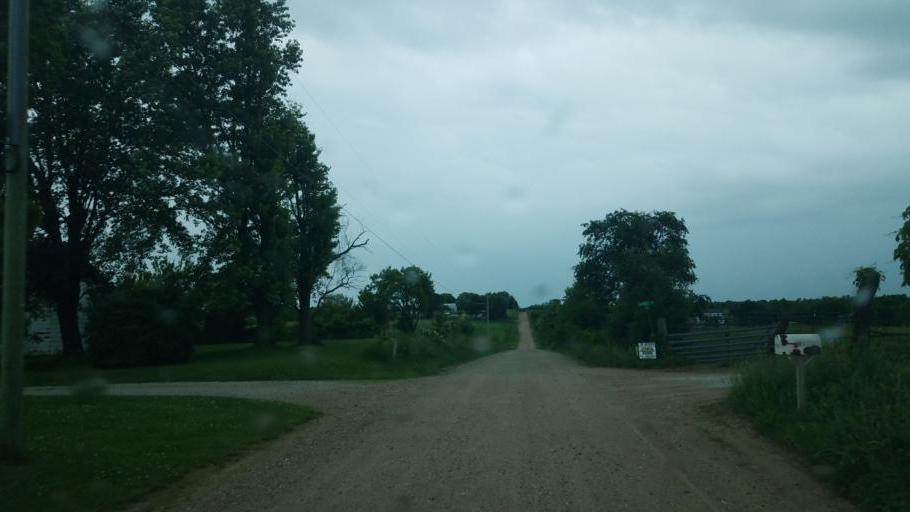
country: US
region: Missouri
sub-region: Moniteau County
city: California
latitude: 38.7529
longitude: -92.6057
